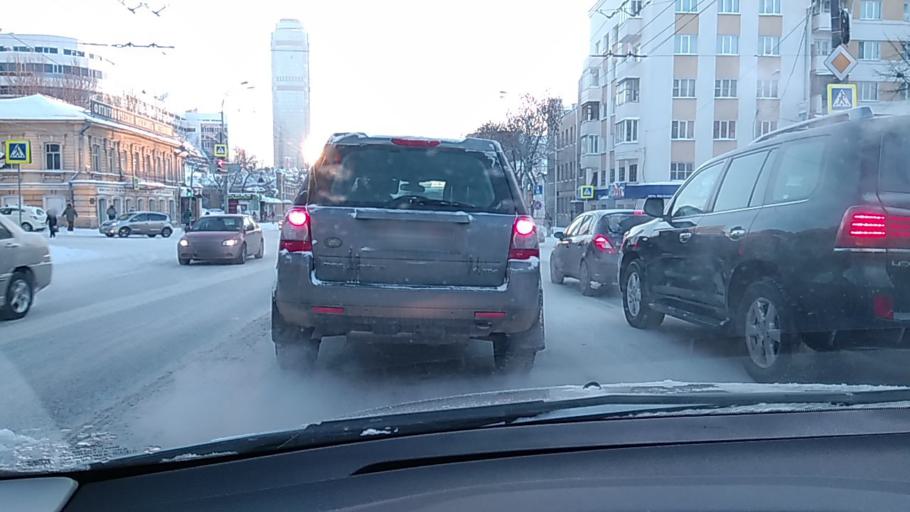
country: RU
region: Sverdlovsk
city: Yekaterinburg
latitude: 56.8424
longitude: 60.6104
